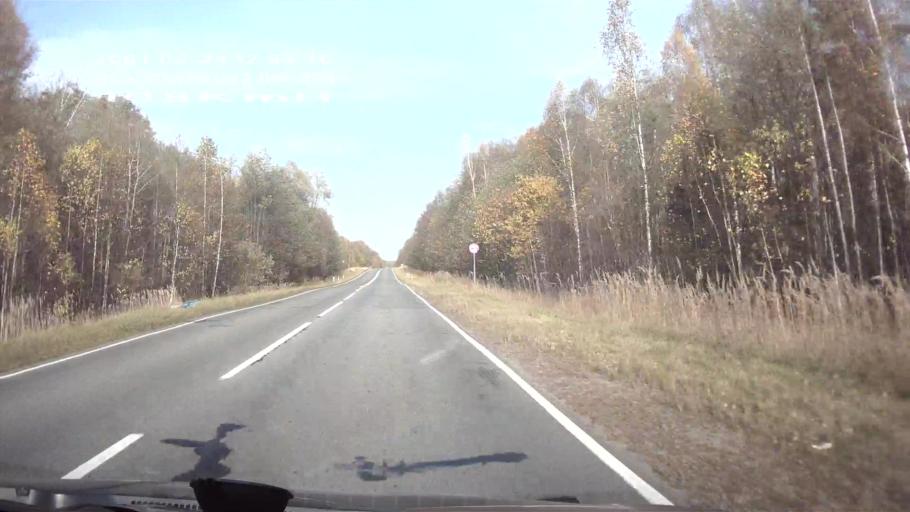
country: RU
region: Chuvashia
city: Buinsk
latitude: 55.1763
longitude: 47.0607
